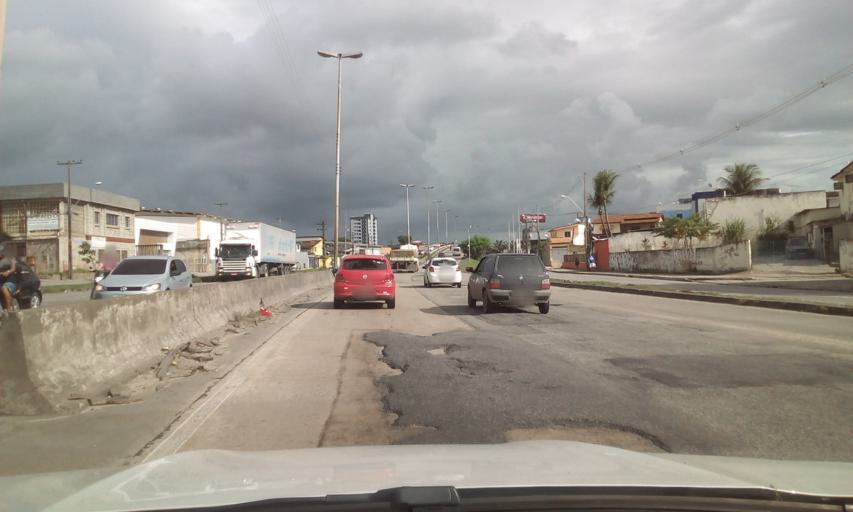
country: BR
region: Pernambuco
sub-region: Recife
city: Recife
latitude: -8.0360
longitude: -34.9415
